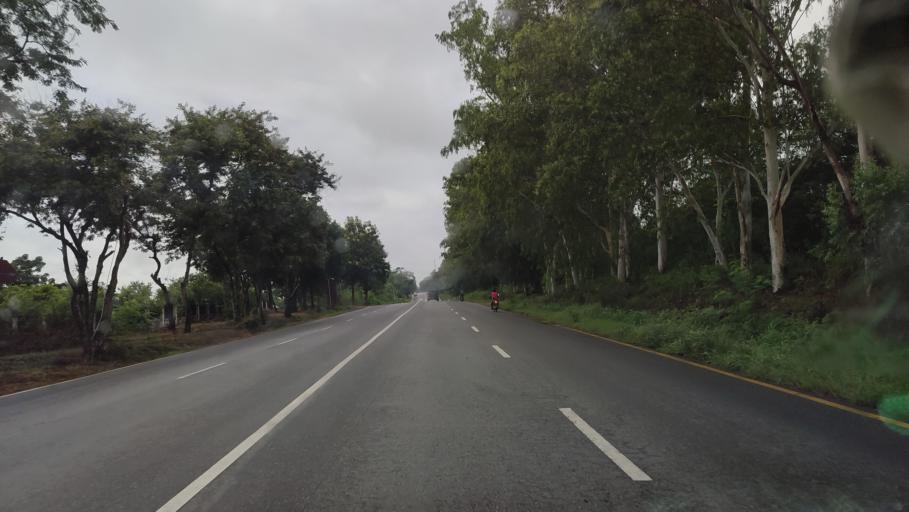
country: MM
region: Mandalay
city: Pyinmana
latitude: 19.9789
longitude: 96.2507
